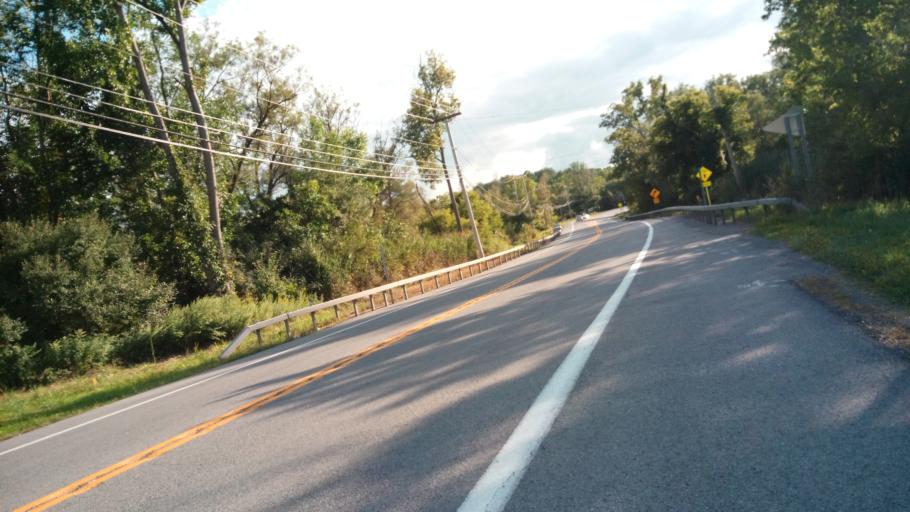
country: US
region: New York
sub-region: Ontario County
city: Victor
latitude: 42.9940
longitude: -77.4353
